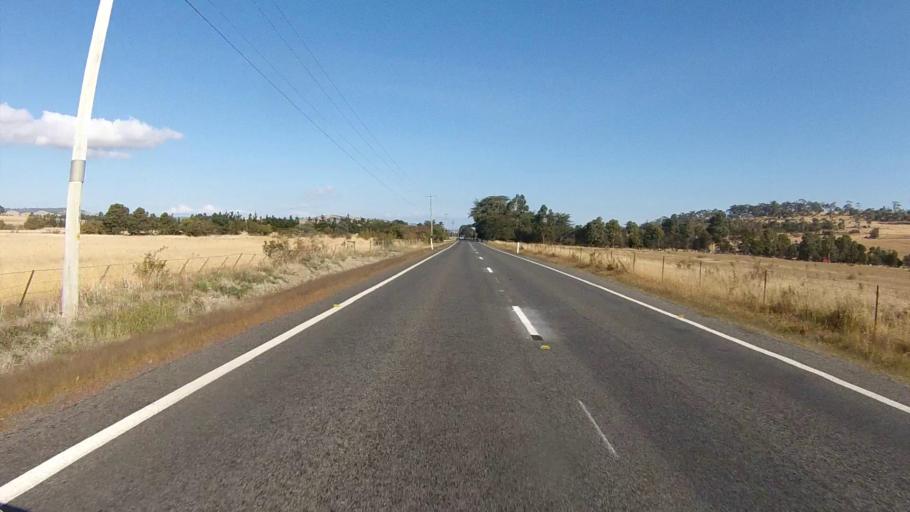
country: AU
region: Tasmania
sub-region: Sorell
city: Sorell
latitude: -42.7223
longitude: 147.5210
